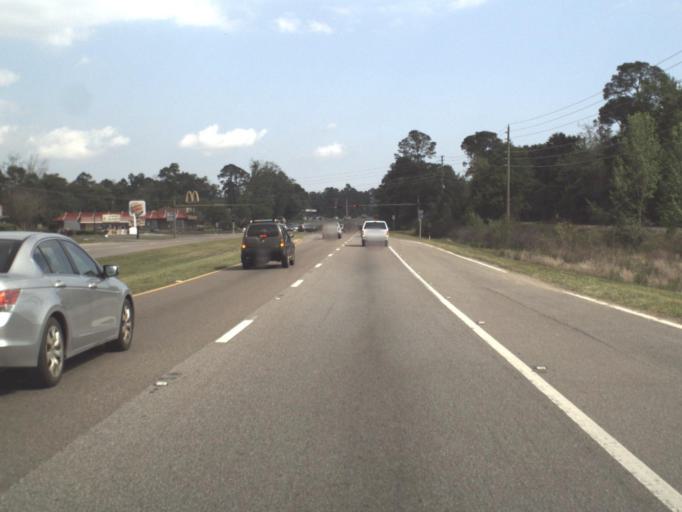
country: US
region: Florida
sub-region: Escambia County
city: Gonzalez
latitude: 30.5802
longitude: -87.2974
